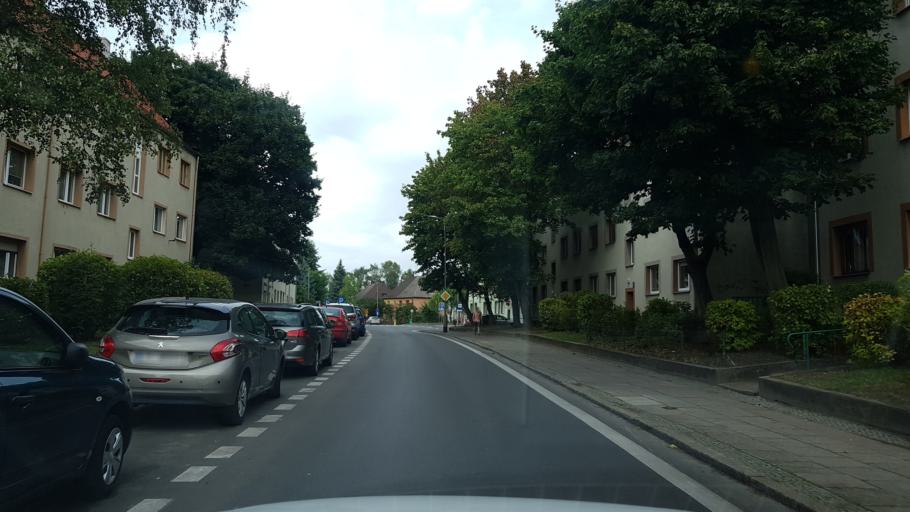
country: PL
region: West Pomeranian Voivodeship
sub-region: Szczecin
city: Szczecin
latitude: 53.4351
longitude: 14.5013
